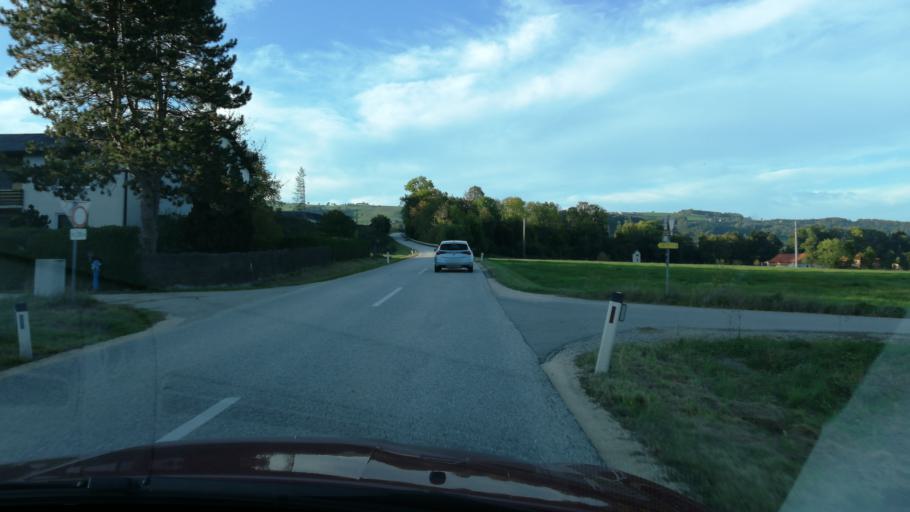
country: AT
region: Upper Austria
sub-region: Politischer Bezirk Steyr-Land
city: Ternberg
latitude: 47.9623
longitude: 14.3477
